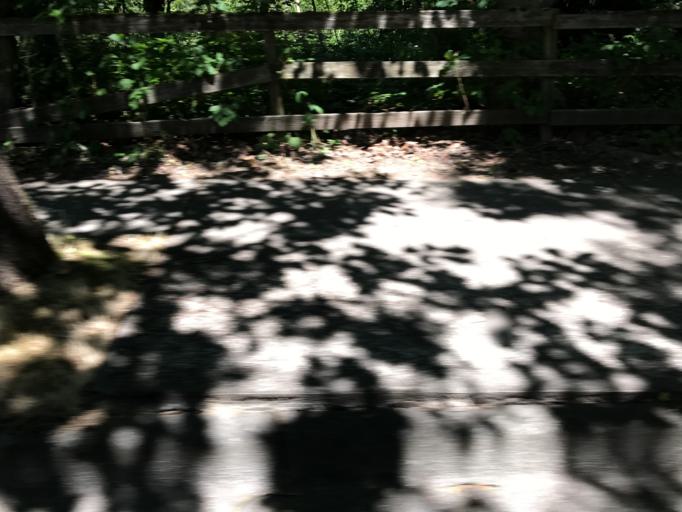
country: US
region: Washington
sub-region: King County
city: Redmond
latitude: 47.6460
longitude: -122.1225
